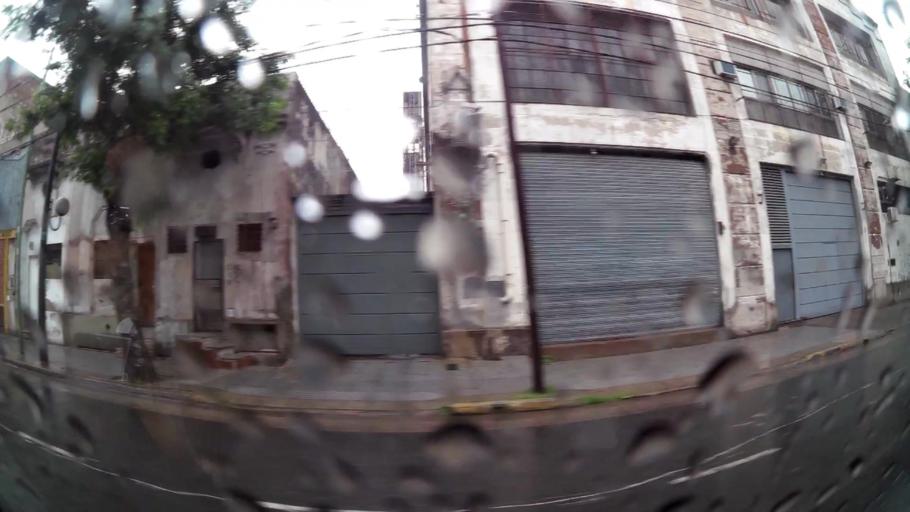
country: AR
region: Buenos Aires F.D.
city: Buenos Aires
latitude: -34.6297
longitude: -58.3586
